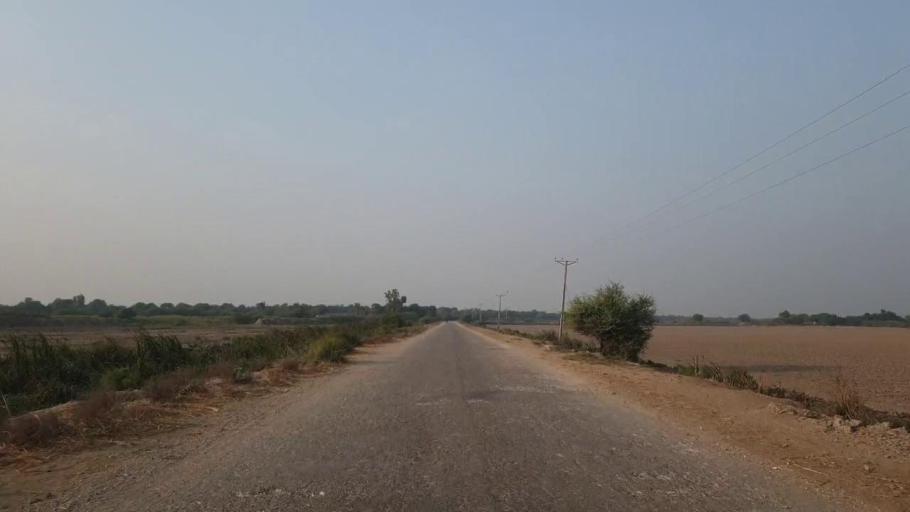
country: PK
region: Sindh
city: Tando Muhammad Khan
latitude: 25.1114
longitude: 68.4288
